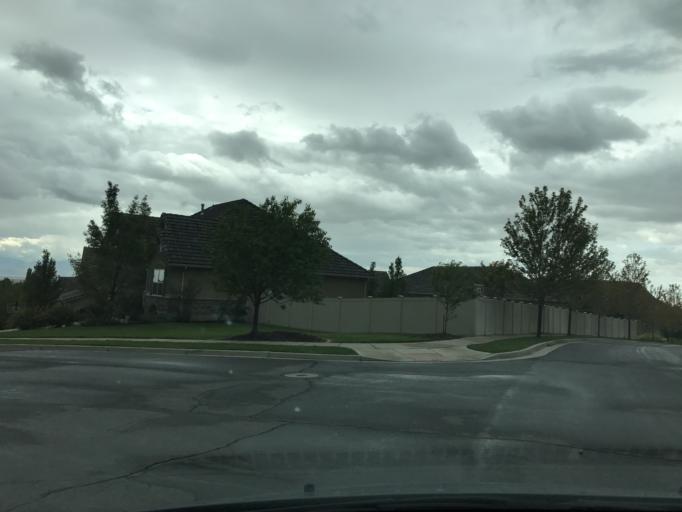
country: US
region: Utah
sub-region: Davis County
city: Fruit Heights
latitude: 41.0189
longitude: -111.9054
